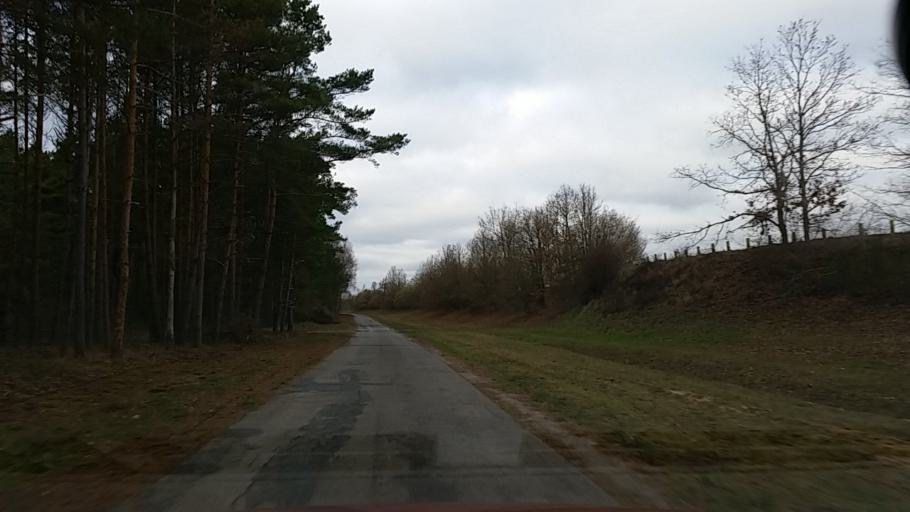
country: DE
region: Lower Saxony
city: Wieren
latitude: 52.8690
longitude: 10.6557
